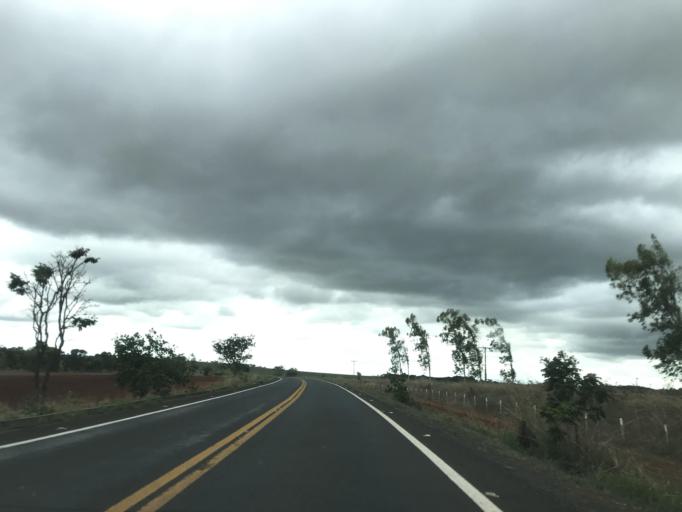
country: BR
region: Goias
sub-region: Caldas Novas
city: Caldas Novas
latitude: -17.6435
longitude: -48.7043
